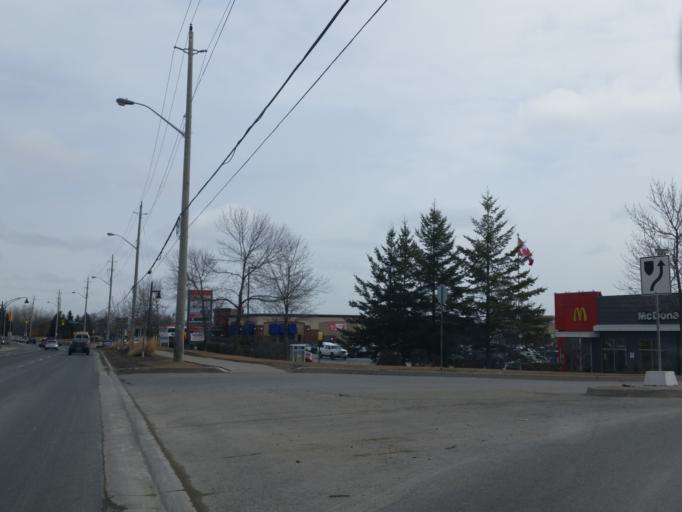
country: CA
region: Ontario
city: Oshawa
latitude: 43.9095
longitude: -78.7096
